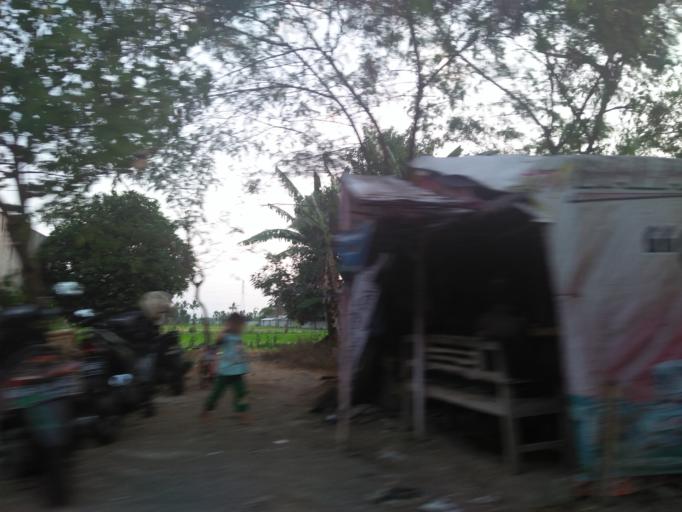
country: ID
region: Daerah Istimewa Yogyakarta
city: Sewon
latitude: -7.8457
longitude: 110.4035
